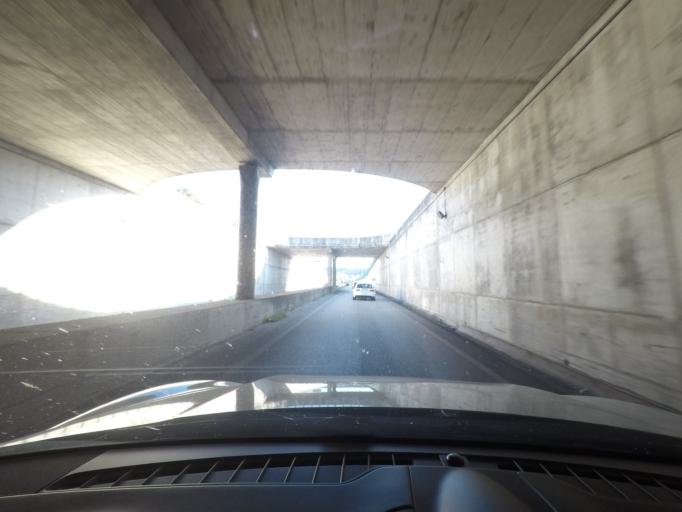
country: PT
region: Coimbra
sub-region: Coimbra
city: Coimbra
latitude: 40.1910
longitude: -8.4207
